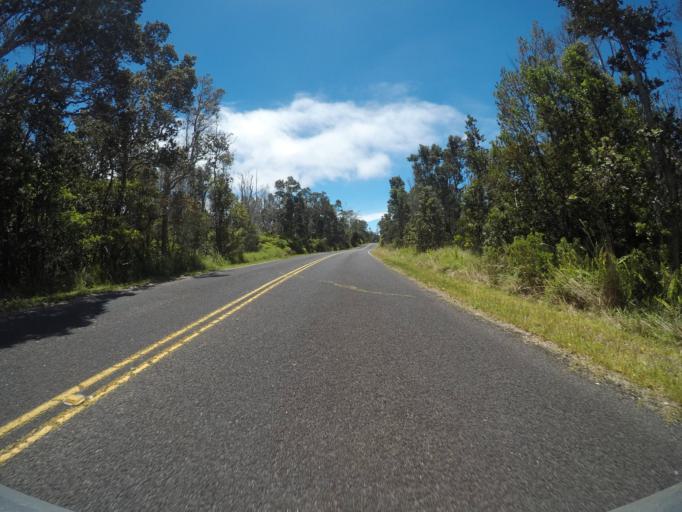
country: US
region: Hawaii
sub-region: Hawaii County
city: Volcano
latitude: 19.3663
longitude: -155.2207
